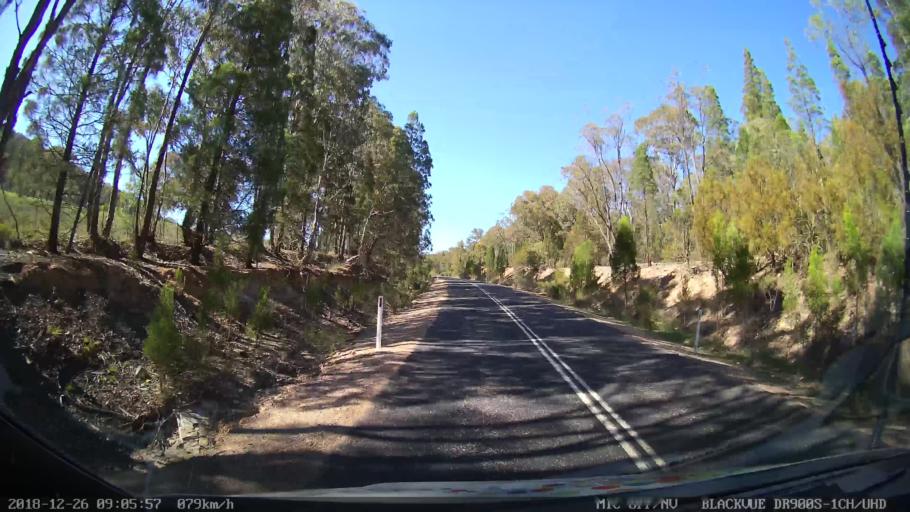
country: AU
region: New South Wales
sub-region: Mid-Western Regional
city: Kandos
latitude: -32.6885
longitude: 150.0048
